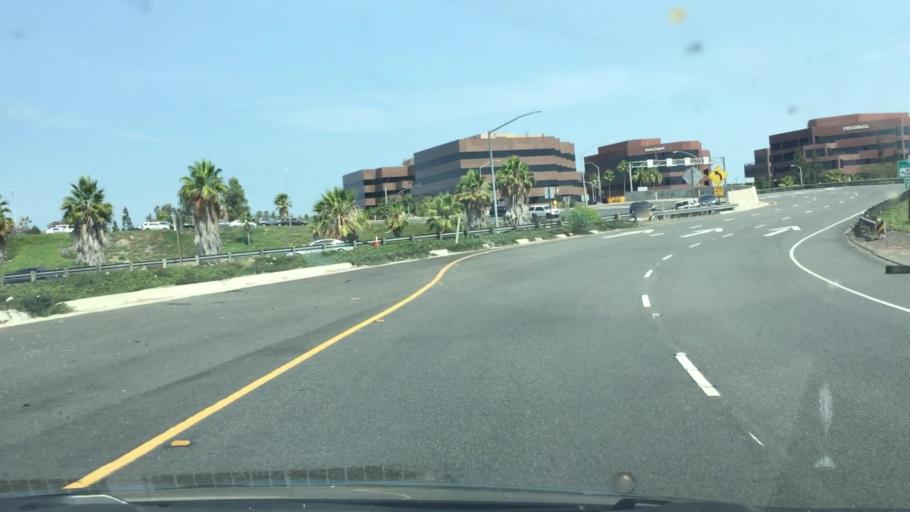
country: US
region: California
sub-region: Orange County
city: Costa Mesa
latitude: 33.6869
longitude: -117.8874
